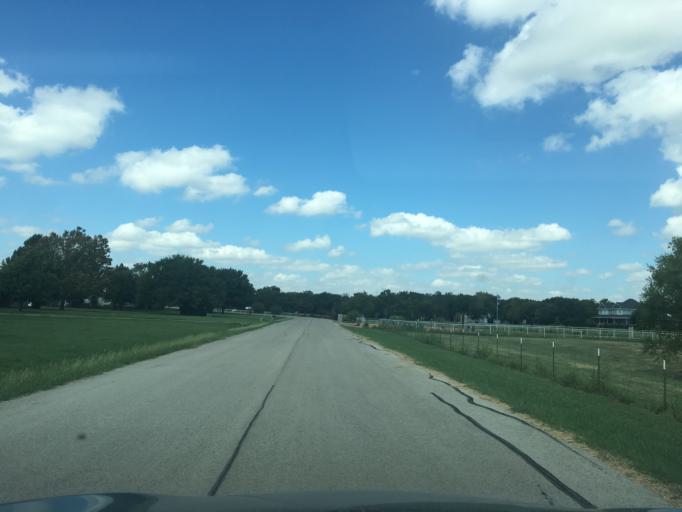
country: US
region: Texas
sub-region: Dallas County
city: Sachse
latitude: 32.9529
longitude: -96.5563
